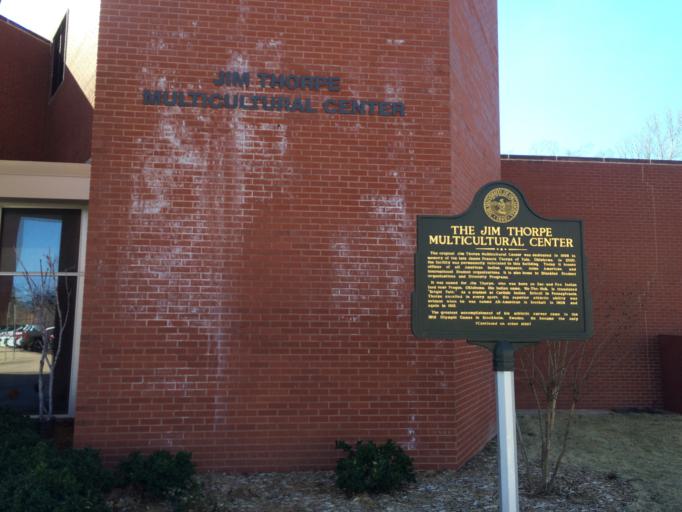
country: US
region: Oklahoma
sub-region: Cleveland County
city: Norman
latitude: 35.1990
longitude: -97.4458
